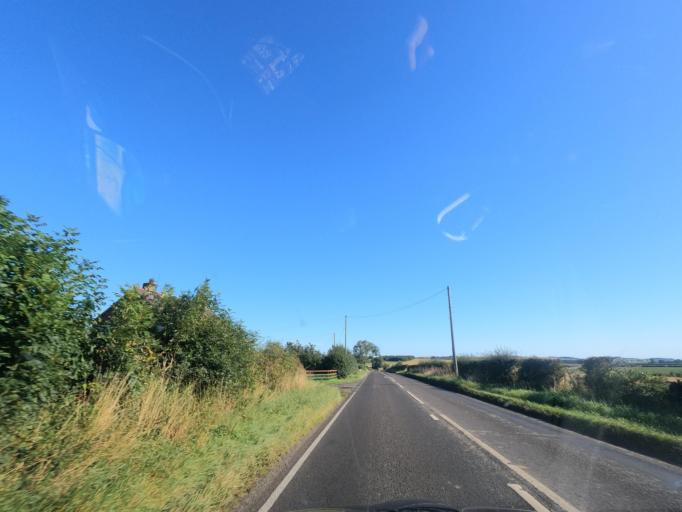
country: GB
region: England
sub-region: Northumberland
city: Ford
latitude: 55.7208
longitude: -2.1026
